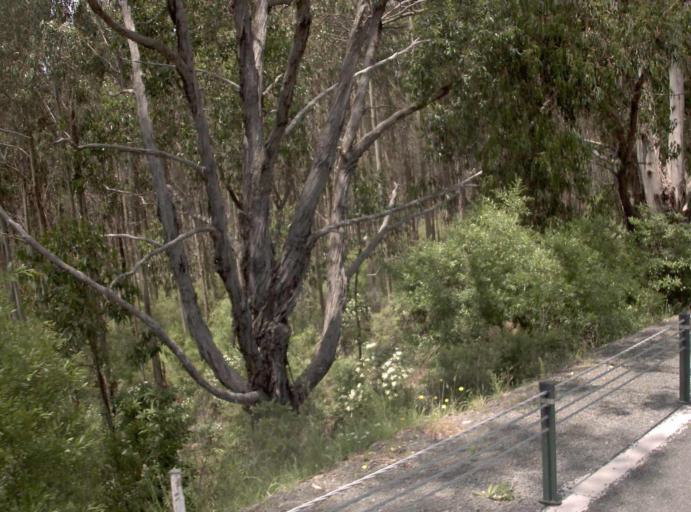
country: AU
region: Victoria
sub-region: Latrobe
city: Traralgon
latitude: -38.3693
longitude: 146.7576
